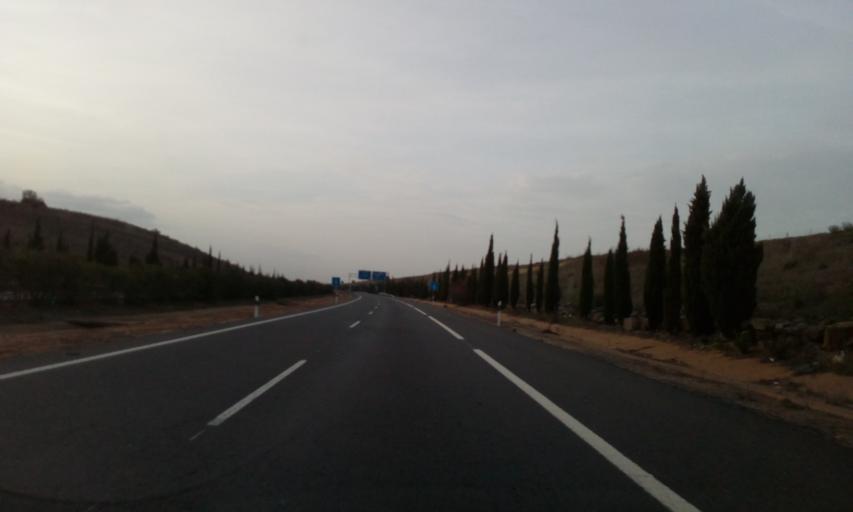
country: ES
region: Andalusia
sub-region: Provincia de Huelva
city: Gibraleon
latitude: 37.3555
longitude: -6.9398
